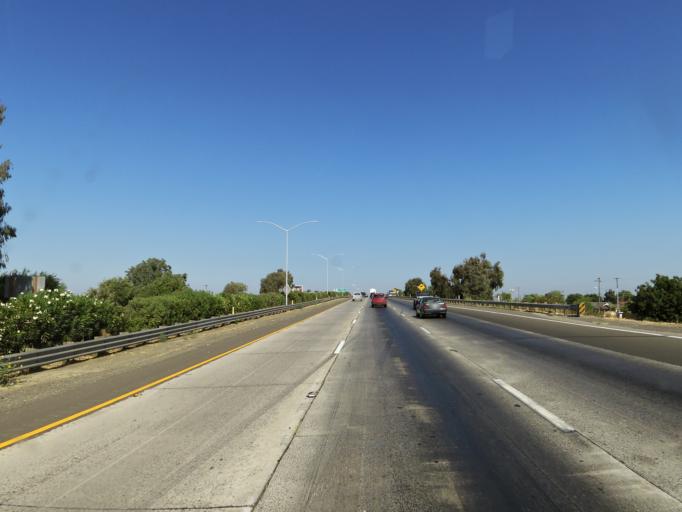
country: US
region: California
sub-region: Stanislaus County
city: Shackelford
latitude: 37.6171
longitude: -120.9899
